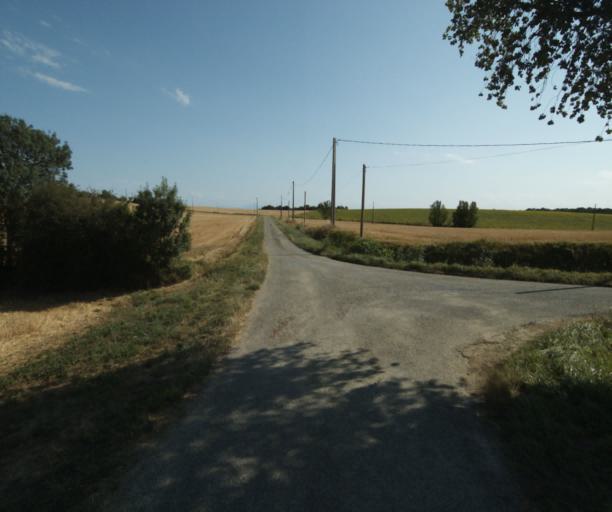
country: FR
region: Midi-Pyrenees
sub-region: Departement de la Haute-Garonne
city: Avignonet-Lauragais
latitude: 43.4192
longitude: 1.8166
